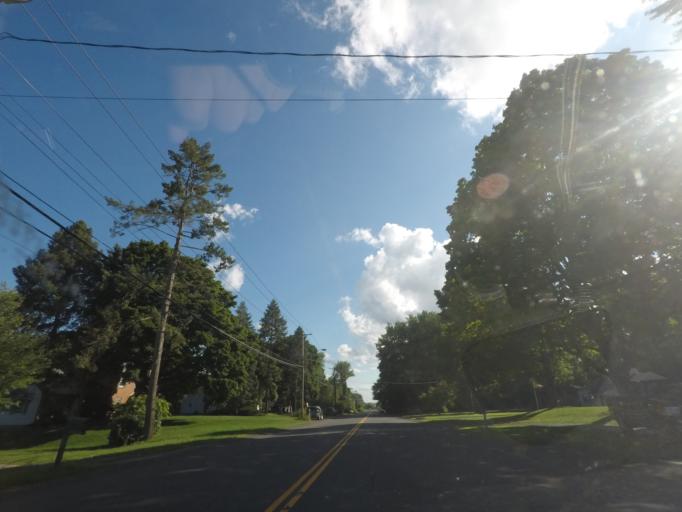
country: US
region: New York
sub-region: Albany County
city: Albany
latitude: 42.6740
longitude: -73.7446
